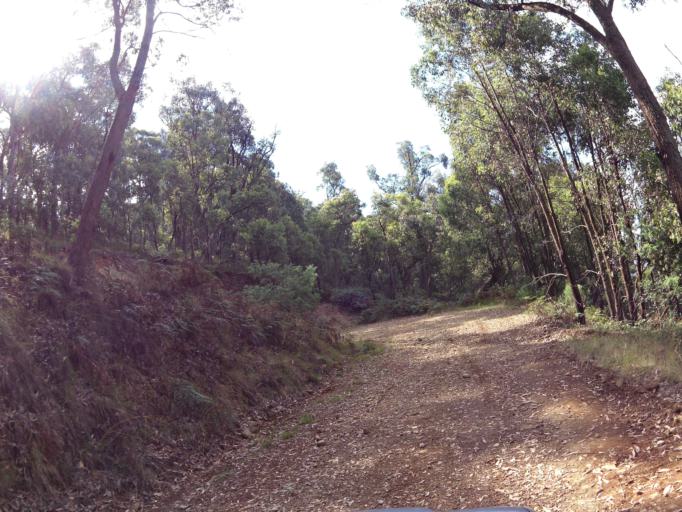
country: AU
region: Victoria
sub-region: Alpine
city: Mount Beauty
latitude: -36.7779
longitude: 147.0102
